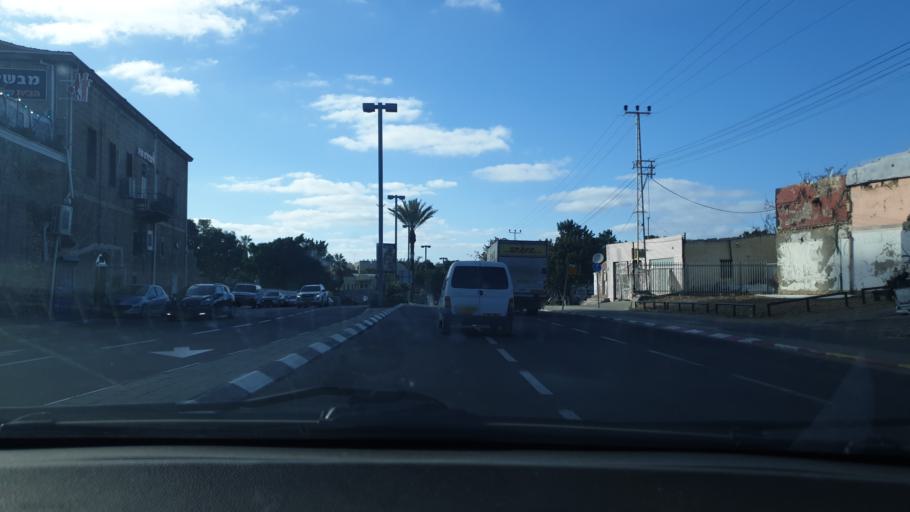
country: IL
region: Tel Aviv
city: Yafo
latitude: 32.0432
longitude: 34.7705
